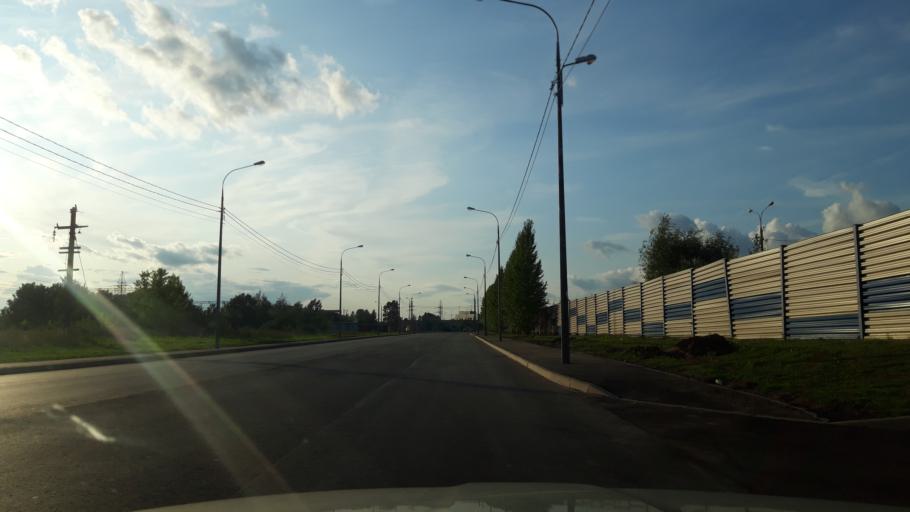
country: RU
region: Moskovskaya
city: Alabushevo
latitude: 56.0066
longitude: 37.1441
